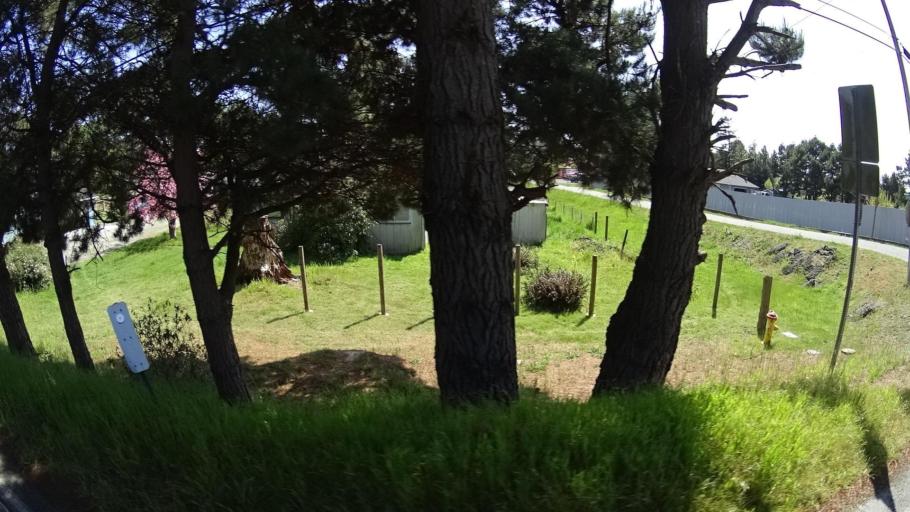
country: US
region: California
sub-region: Humboldt County
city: Hydesville
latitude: 40.5494
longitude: -124.1050
